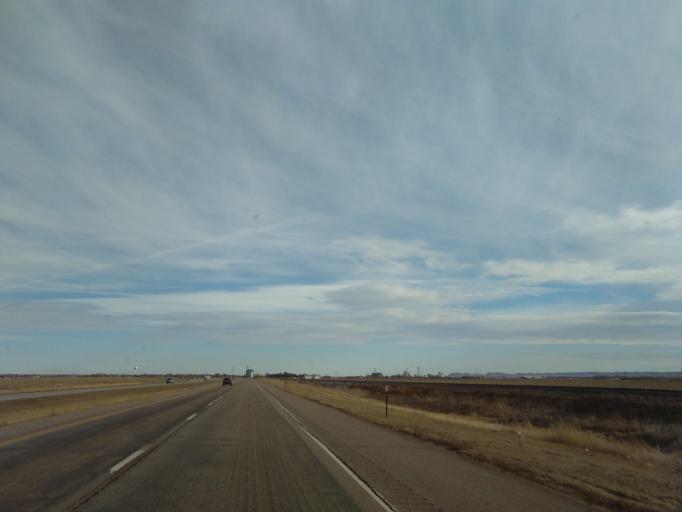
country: US
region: Nebraska
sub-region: Scotts Bluff County
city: Gering
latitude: 41.8188
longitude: -103.5383
